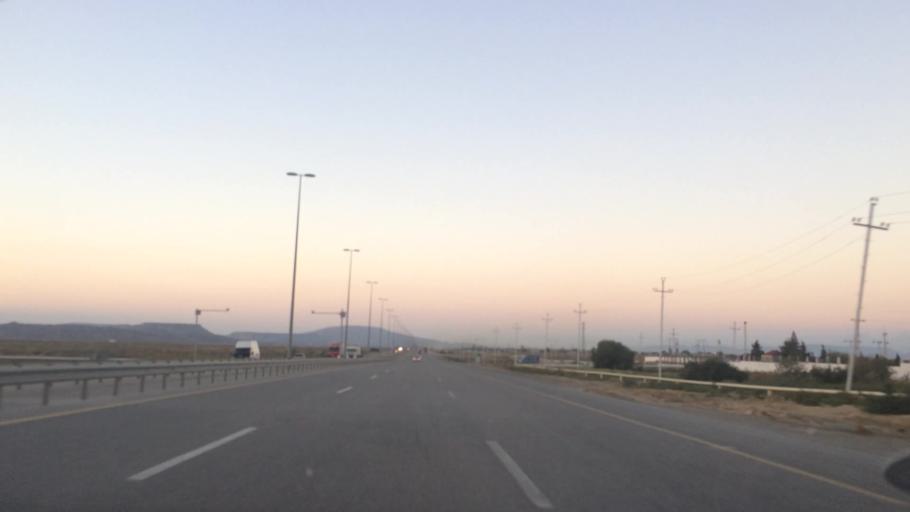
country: AZ
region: Baki
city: Qobustan
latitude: 40.0015
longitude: 49.4299
